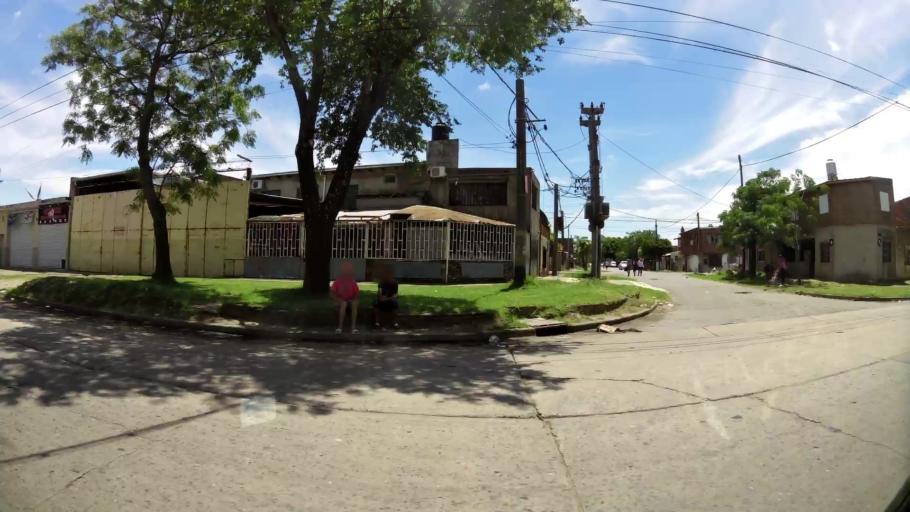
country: AR
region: Santa Fe
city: Gobernador Galvez
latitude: -32.9902
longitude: -60.6332
